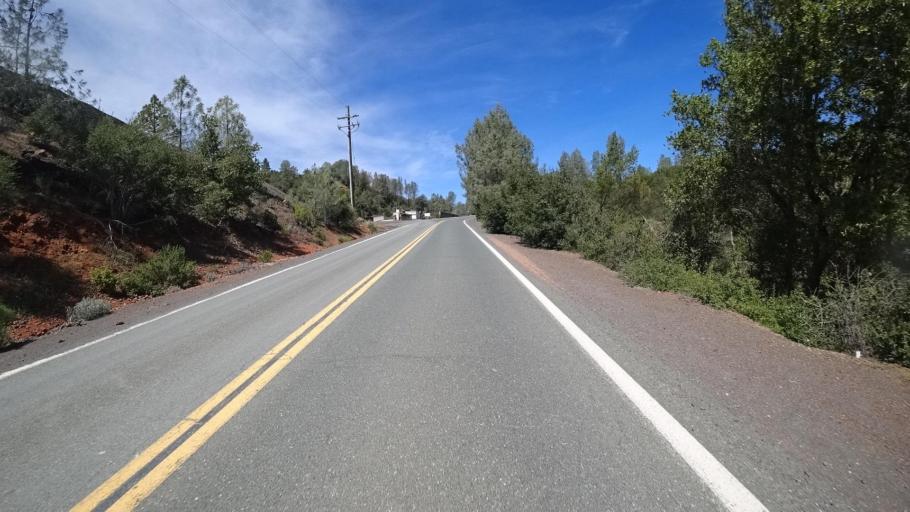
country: US
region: California
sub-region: Lake County
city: Clearlake
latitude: 38.9198
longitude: -122.6630
